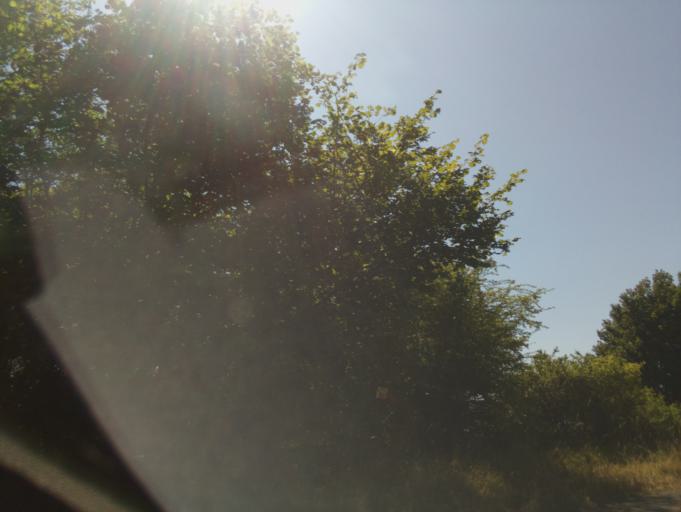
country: GB
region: England
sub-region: South Gloucestershire
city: Tytherington
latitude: 51.5969
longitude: -2.4896
